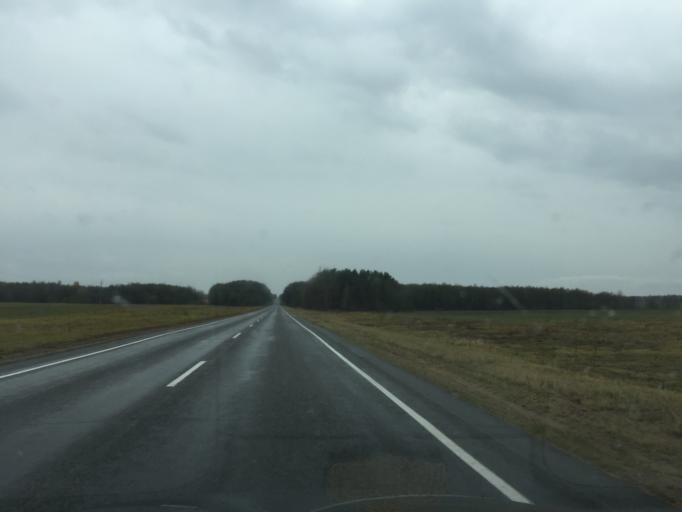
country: BY
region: Mogilev
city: Slawharad
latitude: 53.3893
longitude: 30.8993
